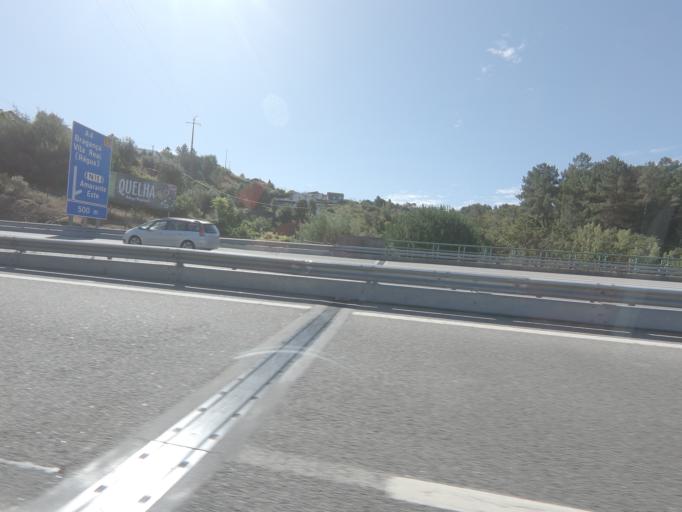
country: PT
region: Porto
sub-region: Amarante
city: Amarante
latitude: 41.2603
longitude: -8.0785
